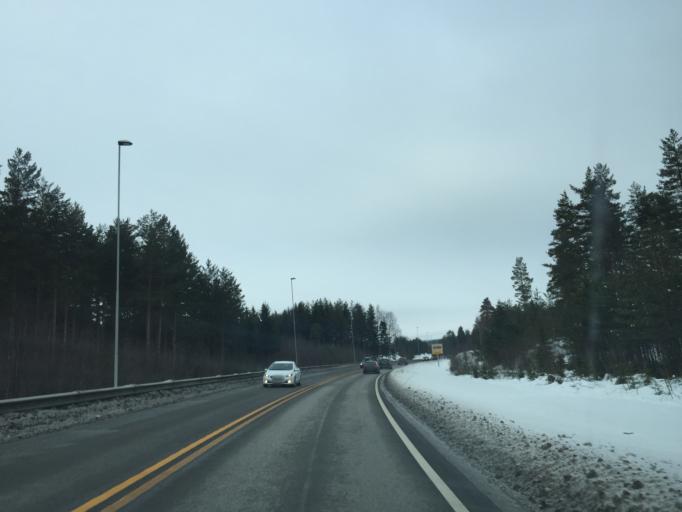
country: NO
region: Hedmark
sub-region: Loten
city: Loten
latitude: 60.7768
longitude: 11.3057
